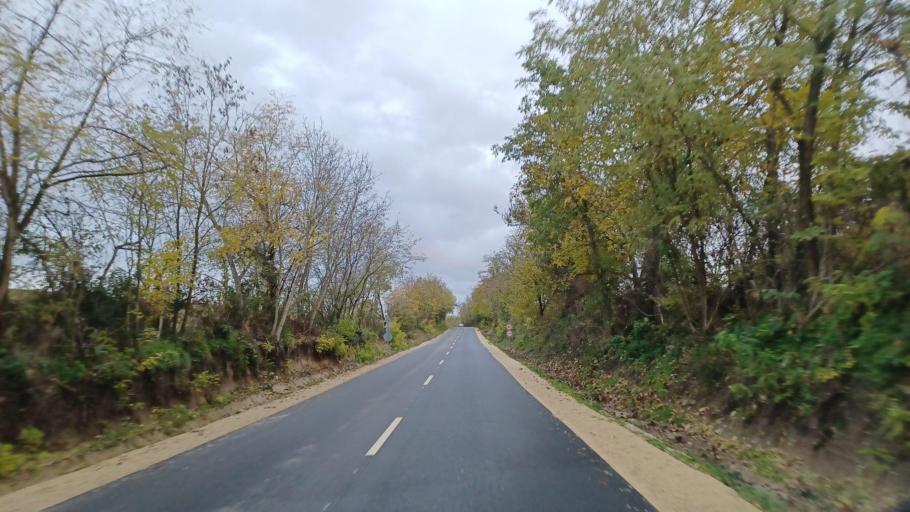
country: HU
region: Tolna
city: Gyonk
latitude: 46.5762
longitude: 18.4577
